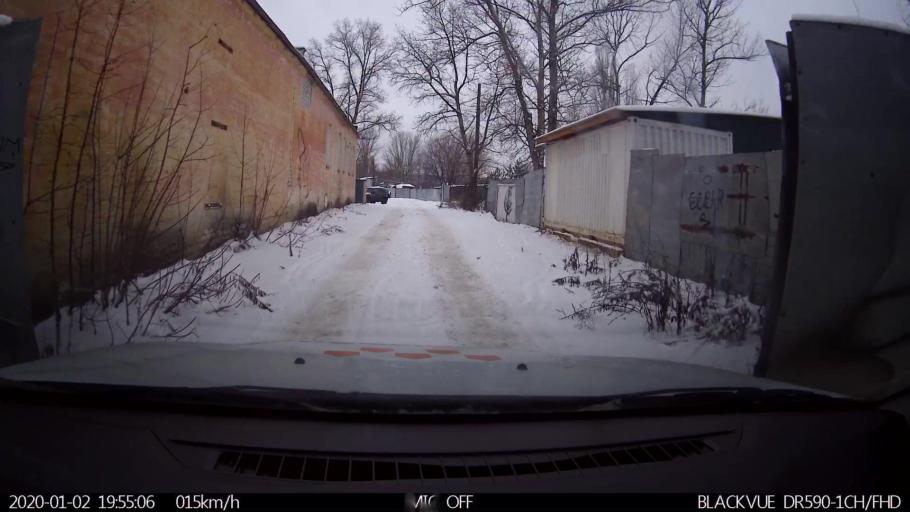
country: RU
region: Nizjnij Novgorod
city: Nizhniy Novgorod
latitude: 56.2745
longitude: 43.9593
